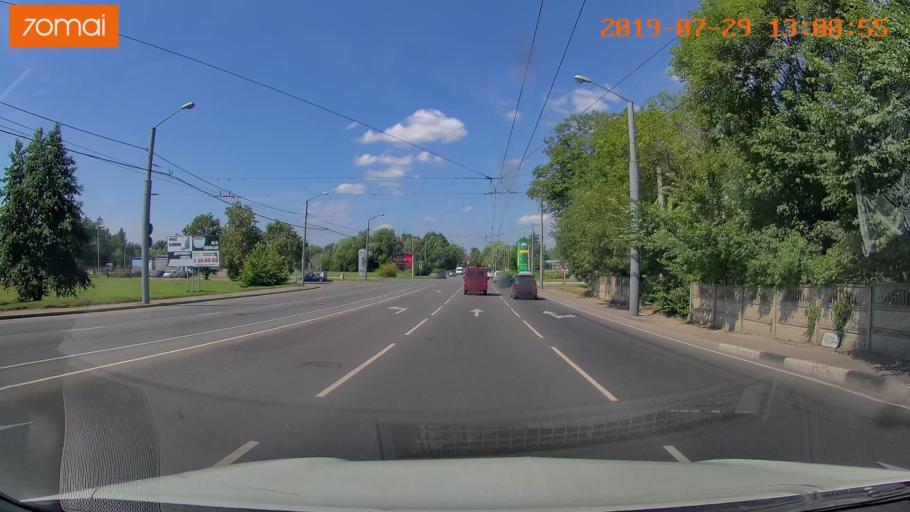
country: RU
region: Kaliningrad
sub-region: Gorod Kaliningrad
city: Kaliningrad
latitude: 54.7126
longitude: 20.4240
